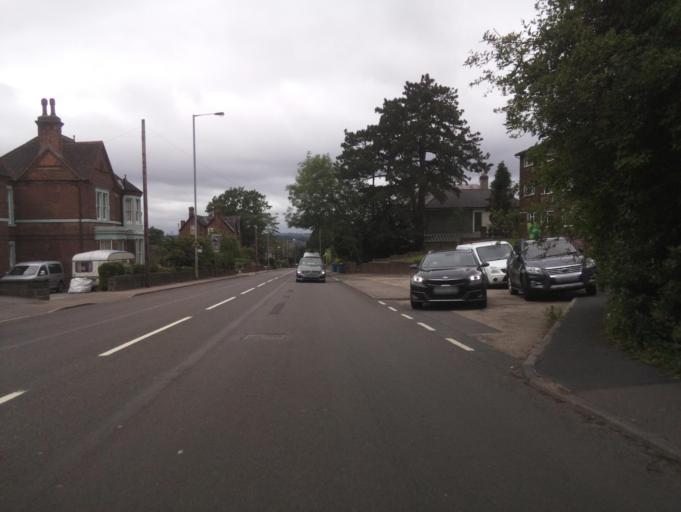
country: GB
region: England
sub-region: Staffordshire
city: Burton upon Trent
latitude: 52.8044
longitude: -1.6122
